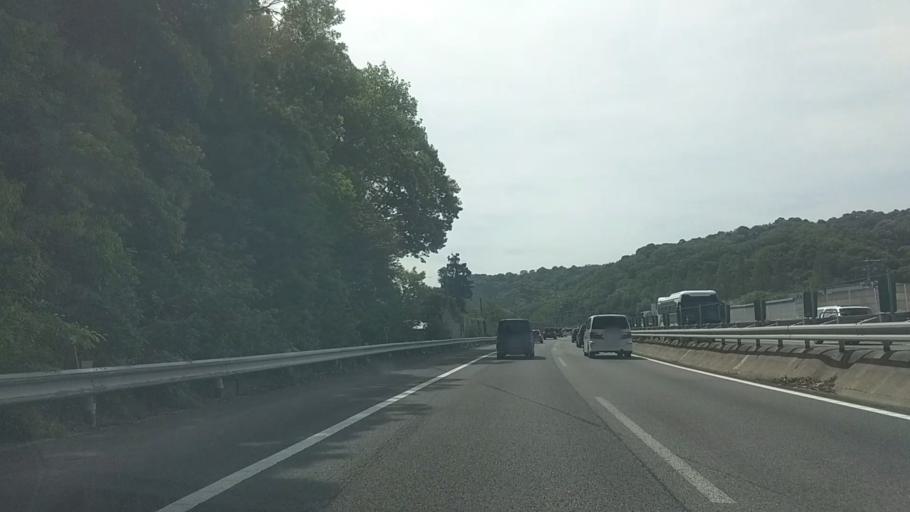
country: JP
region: Aichi
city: Okazaki
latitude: 34.9304
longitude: 137.2216
